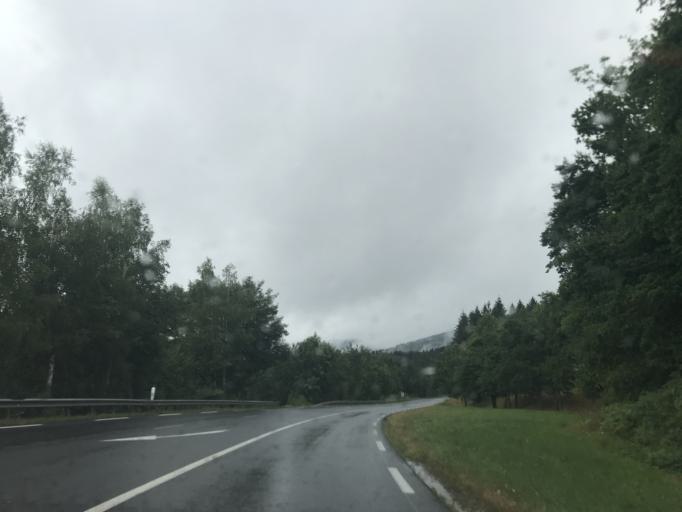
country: FR
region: Auvergne
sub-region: Departement du Puy-de-Dome
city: Job
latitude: 45.6309
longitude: 3.7121
